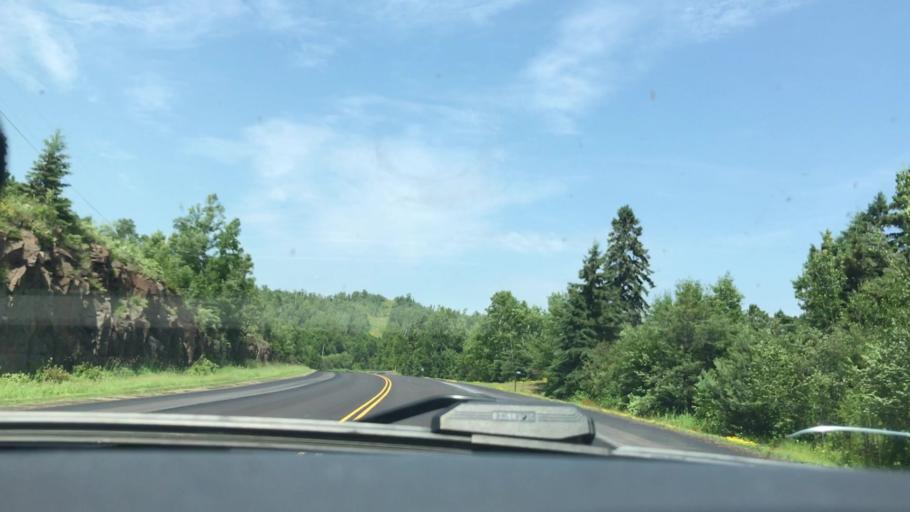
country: US
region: Minnesota
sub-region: Lake County
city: Silver Bay
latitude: 47.3628
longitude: -91.1738
